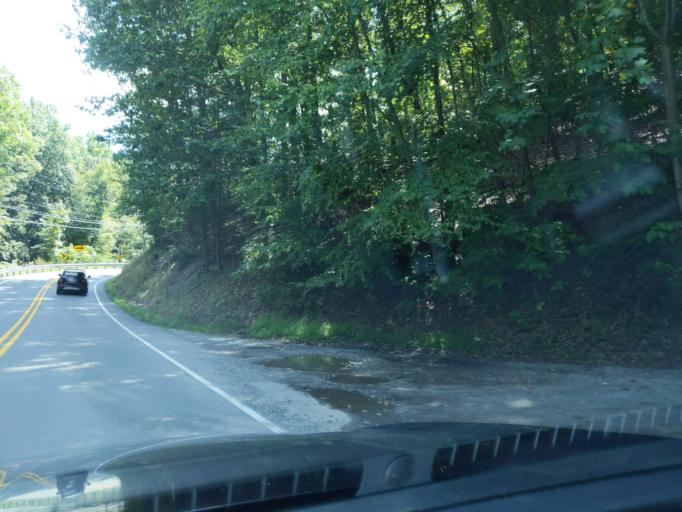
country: US
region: Pennsylvania
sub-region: Blair County
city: Greenwood
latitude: 40.5272
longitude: -78.2994
